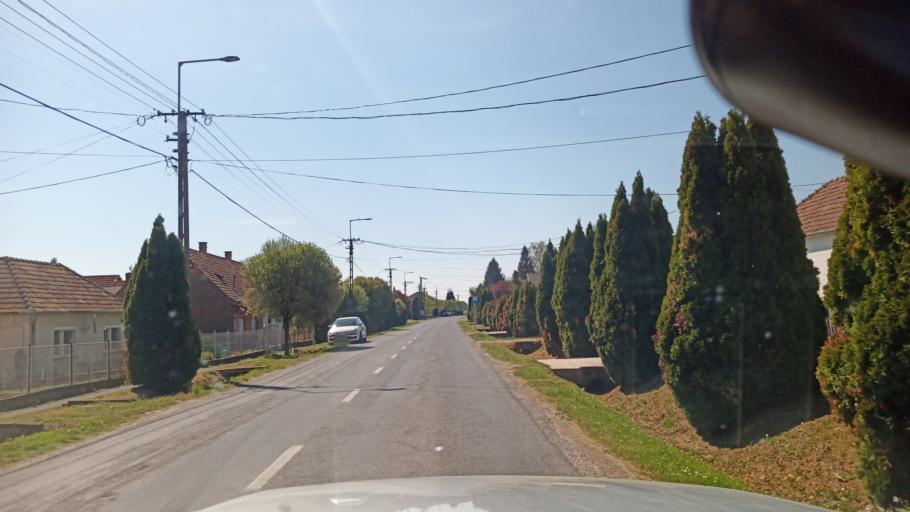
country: HU
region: Zala
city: Sarmellek
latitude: 46.7409
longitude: 17.1064
